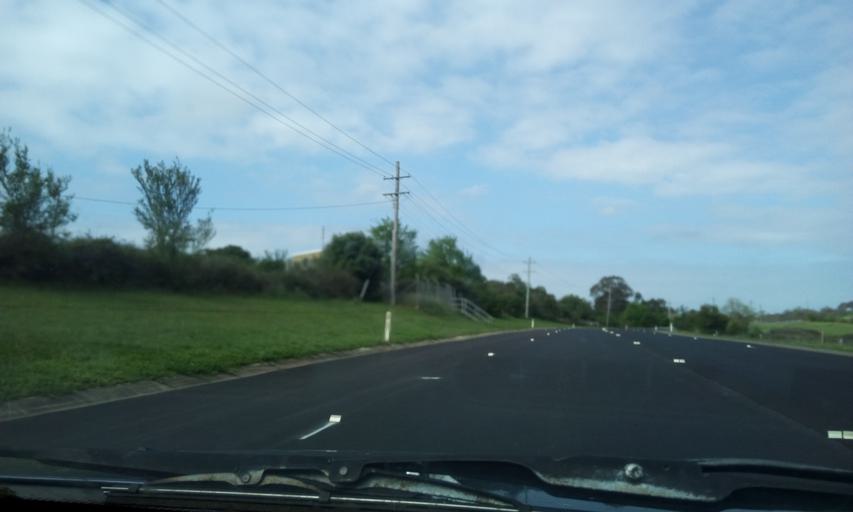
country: AU
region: New South Wales
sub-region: Campbelltown Municipality
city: Glen Alpine
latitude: -34.1081
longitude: 150.7506
